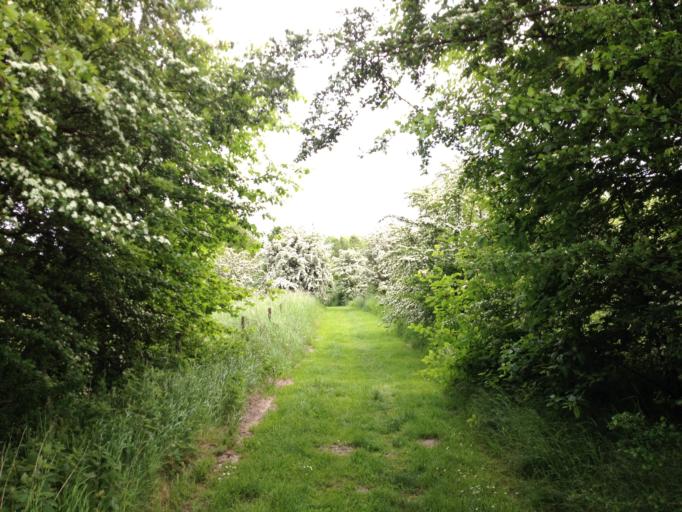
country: DK
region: Capital Region
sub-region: Fredensborg Kommune
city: Niva
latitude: 55.9304
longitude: 12.4932
